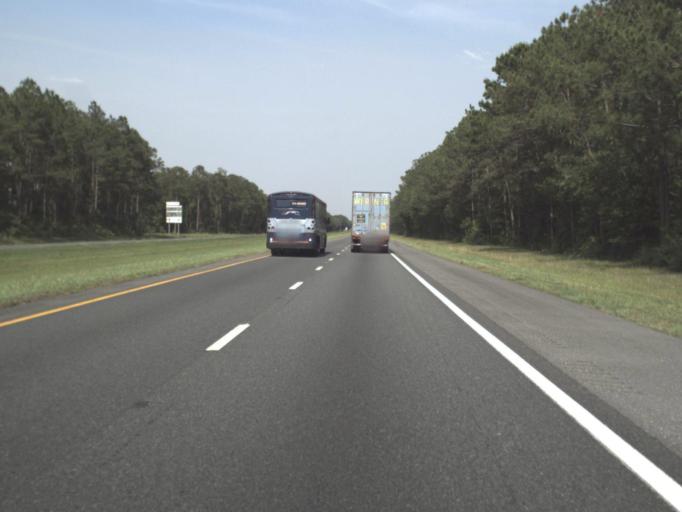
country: US
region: Florida
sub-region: Baker County
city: Macclenny
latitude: 30.2334
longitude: -82.2861
